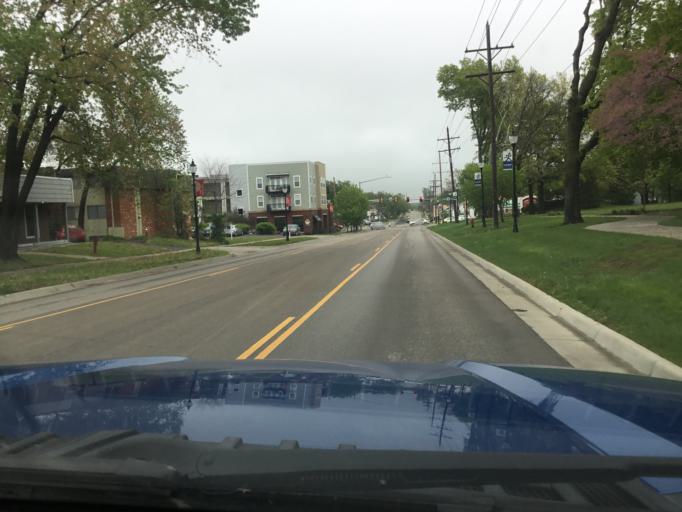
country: US
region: Kansas
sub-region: Shawnee County
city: Topeka
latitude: 39.0369
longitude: -95.6985
